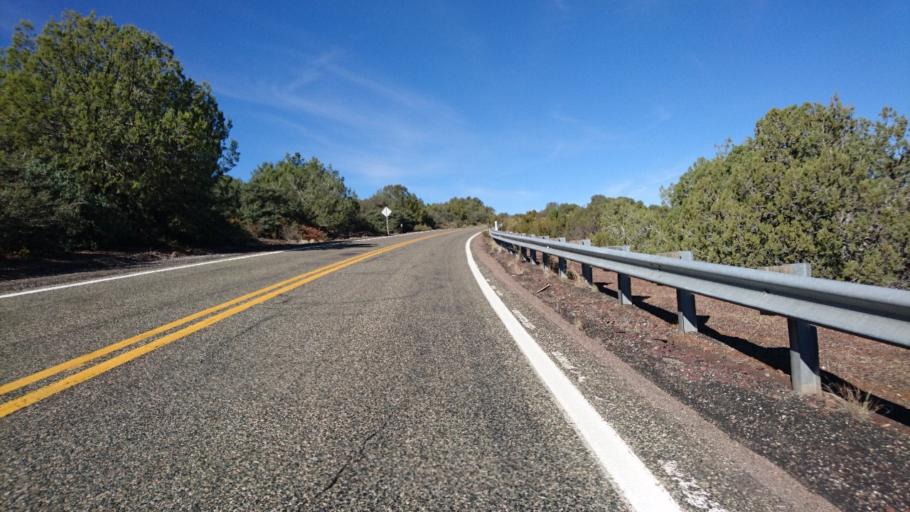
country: US
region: Arizona
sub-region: Yavapai County
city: Paulden
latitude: 35.2780
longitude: -112.6957
